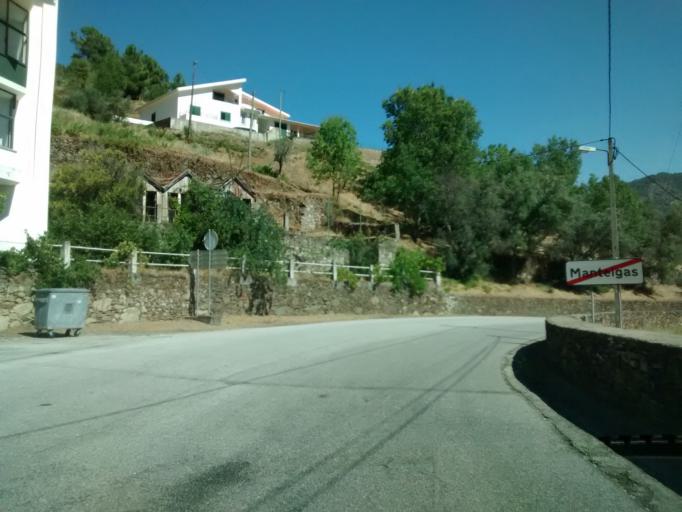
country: PT
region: Guarda
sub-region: Manteigas
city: Manteigas
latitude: 40.4065
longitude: -7.5246
